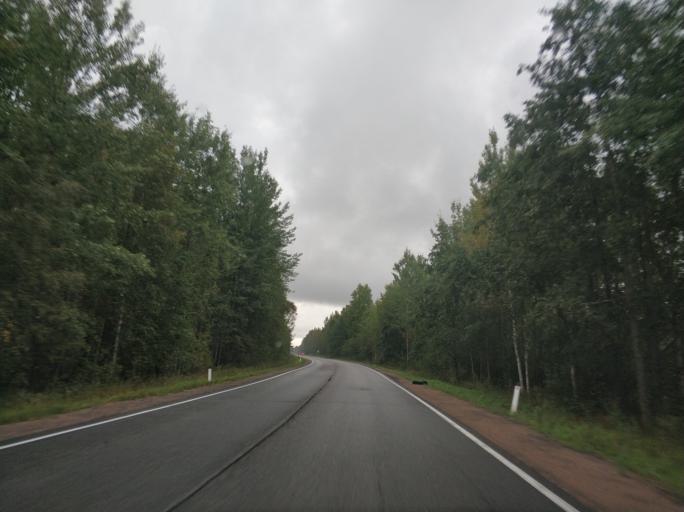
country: RU
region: Leningrad
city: Borisova Griva
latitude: 60.1149
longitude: 30.9636
